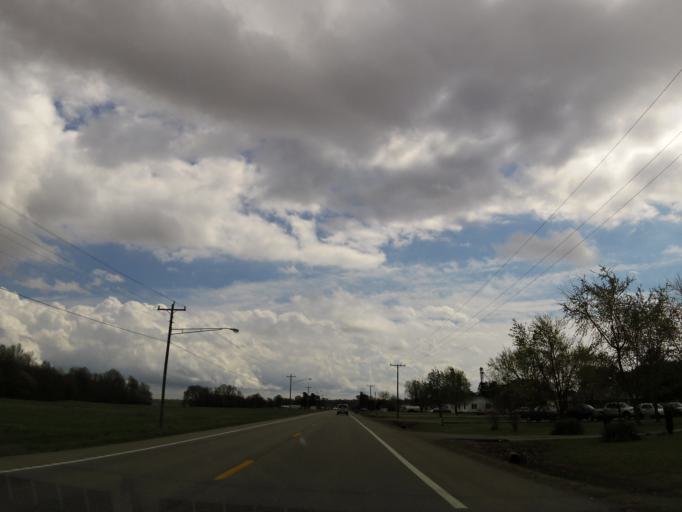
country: US
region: Arkansas
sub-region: Clay County
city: Corning
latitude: 36.4050
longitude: -90.5663
